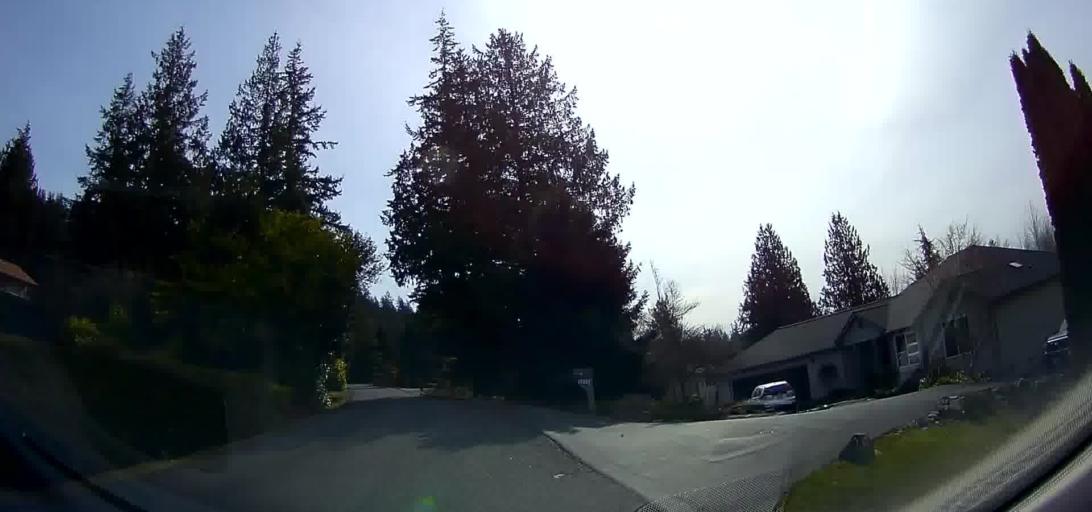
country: US
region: Washington
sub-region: Skagit County
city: Mount Vernon
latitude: 48.3942
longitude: -122.3167
